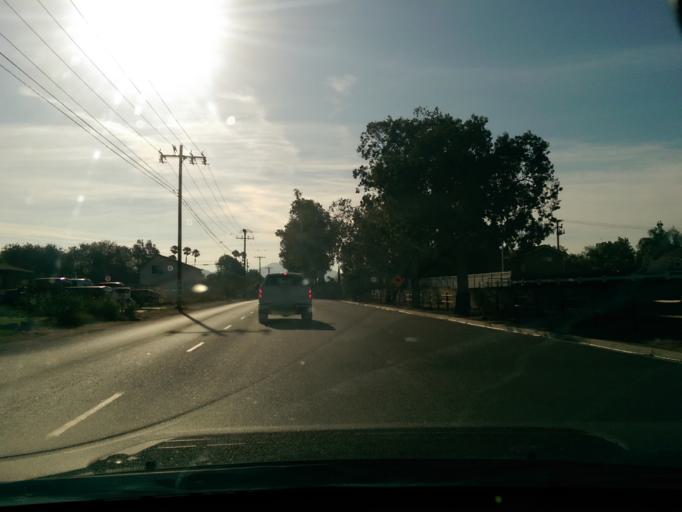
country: US
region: California
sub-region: Riverside County
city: Norco
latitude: 33.9095
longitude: -117.5727
